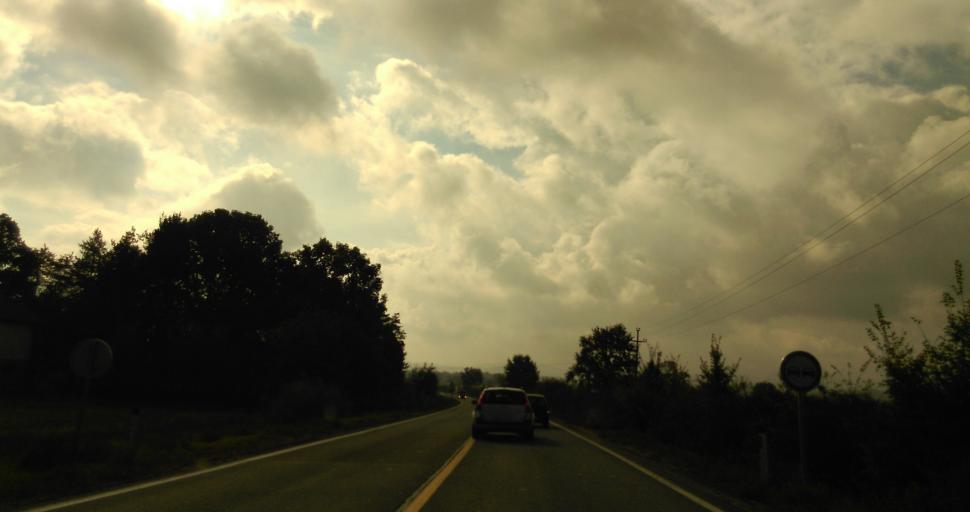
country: RS
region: Central Serbia
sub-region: Kolubarski Okrug
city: Ljig
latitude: 44.2988
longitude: 20.2603
